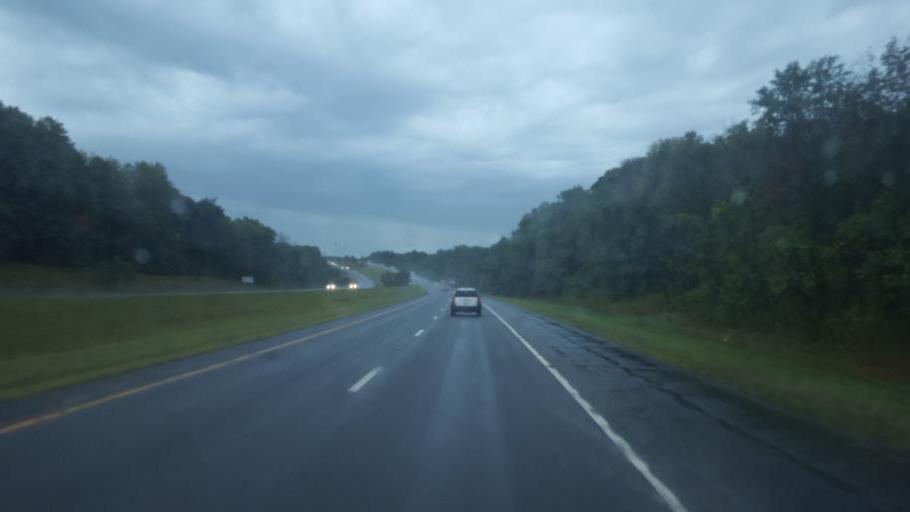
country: US
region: Ohio
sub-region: Medina County
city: Brunswick
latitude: 41.1845
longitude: -81.7562
